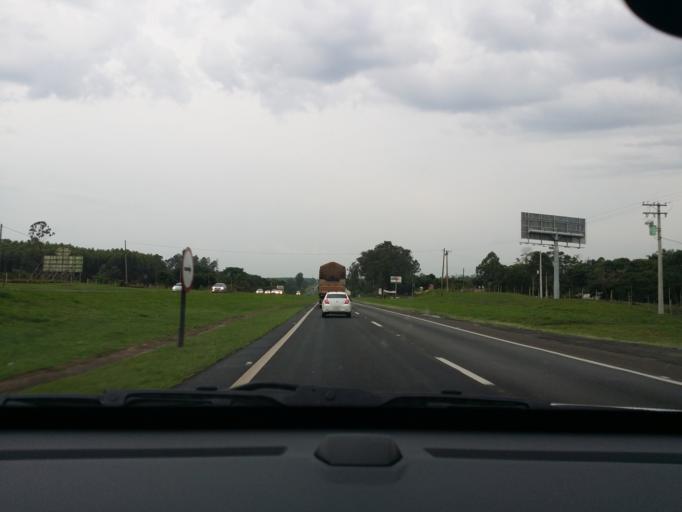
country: BR
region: Sao Paulo
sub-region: Sao Carlos
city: Sao Carlos
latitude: -22.1042
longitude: -47.8240
